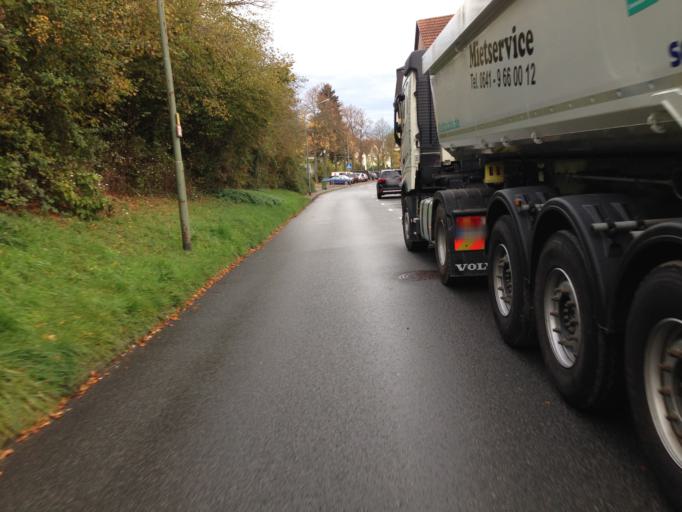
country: DE
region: Hesse
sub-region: Regierungsbezirk Giessen
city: Heuchelheim
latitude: 50.5860
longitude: 8.6334
